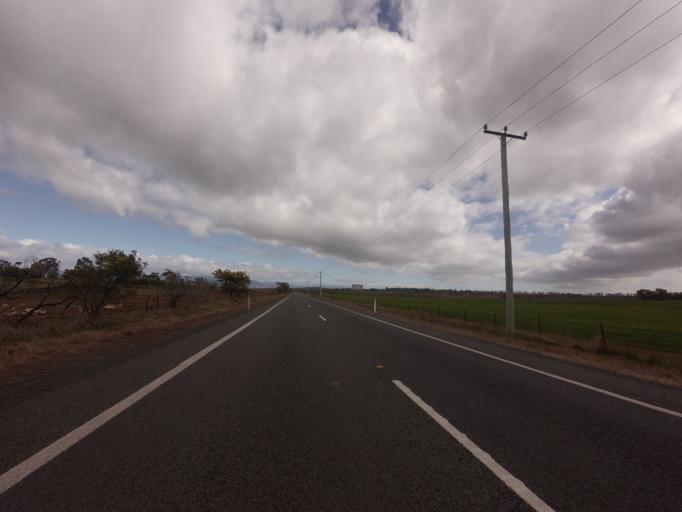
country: AU
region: Tasmania
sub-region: Northern Midlands
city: Evandale
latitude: -41.8342
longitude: 147.4611
